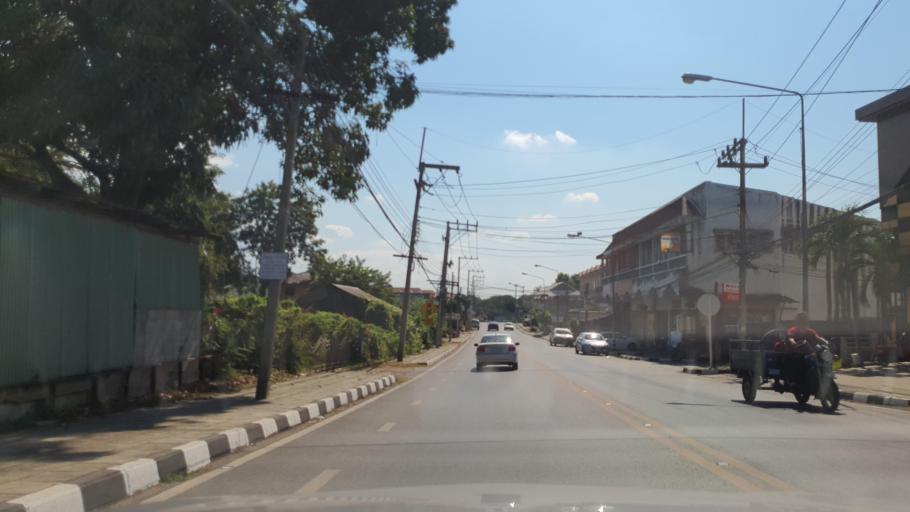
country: TH
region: Nan
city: Nan
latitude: 18.7944
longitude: 100.7796
